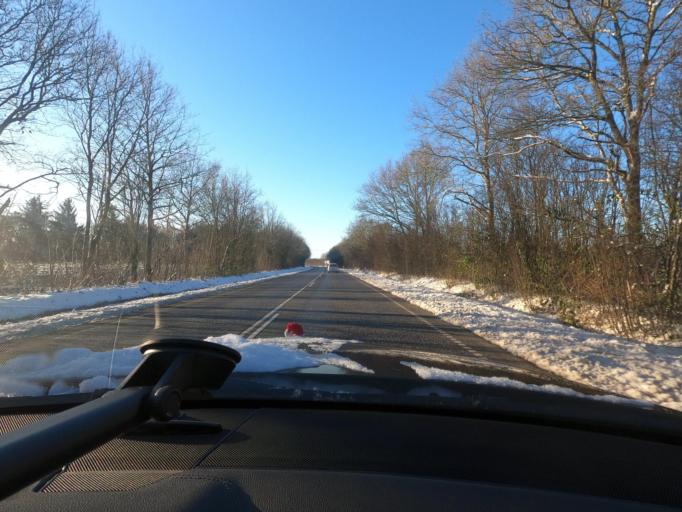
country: DK
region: South Denmark
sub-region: Tonder Kommune
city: Sherrebek
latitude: 55.1717
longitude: 8.7692
